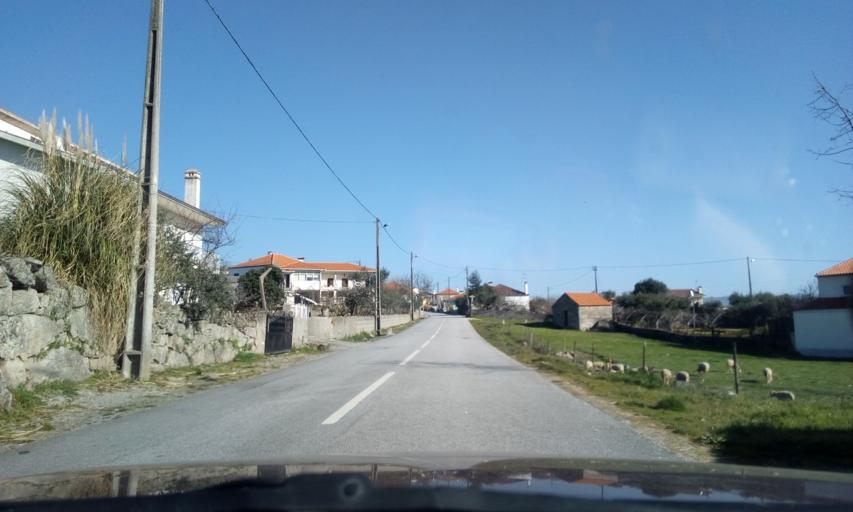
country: PT
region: Guarda
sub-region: Celorico da Beira
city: Celorico da Beira
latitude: 40.6534
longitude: -7.4648
